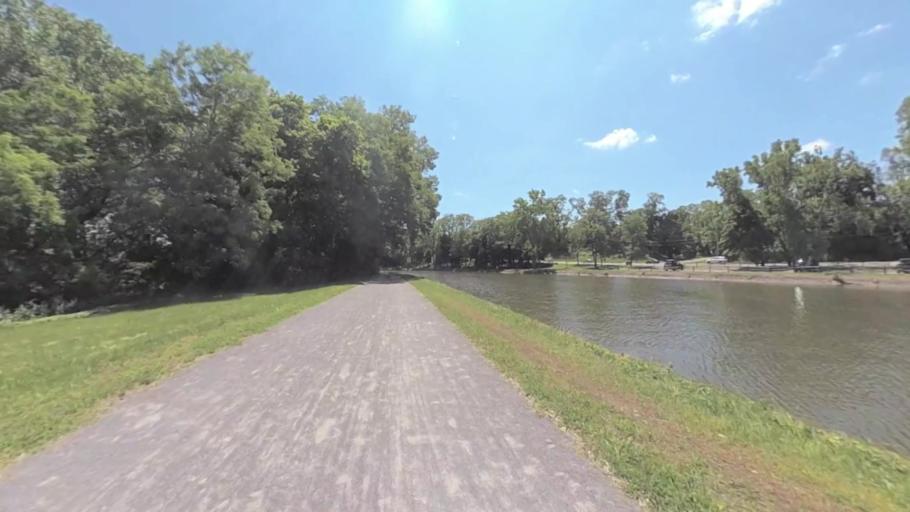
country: US
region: New York
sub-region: Monroe County
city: Pittsford
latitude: 43.0635
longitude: -77.4830
